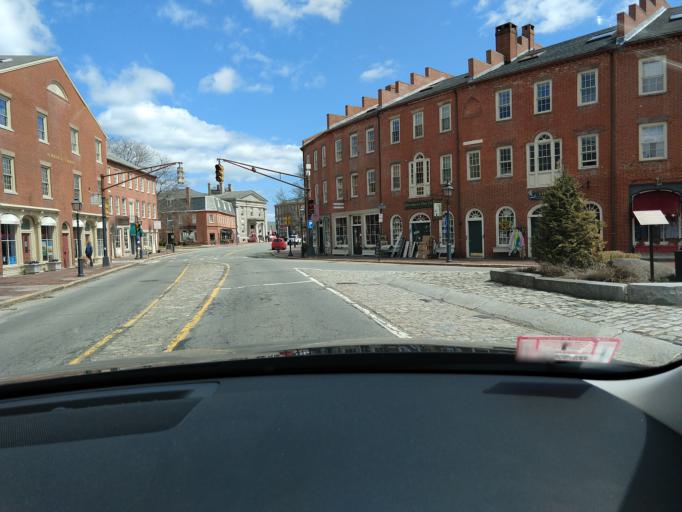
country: US
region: Massachusetts
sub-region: Essex County
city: Newburyport
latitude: 42.8115
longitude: -70.8698
